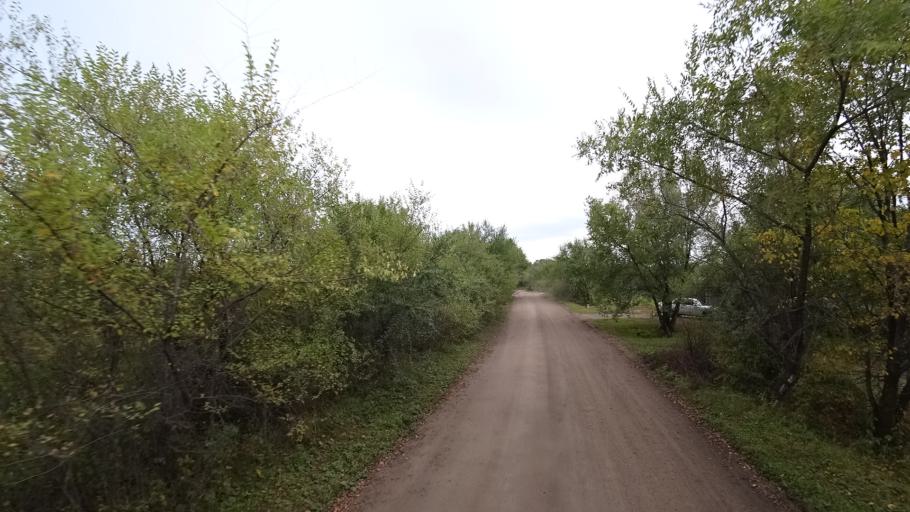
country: RU
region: Amur
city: Arkhara
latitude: 49.3527
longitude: 130.1102
